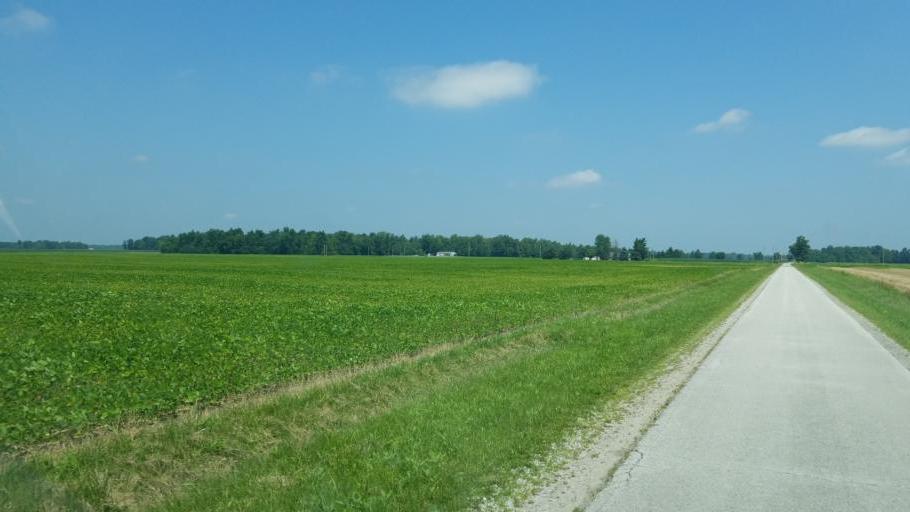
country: US
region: Ohio
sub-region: Crawford County
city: Bucyrus
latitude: 41.0183
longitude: -82.9776
